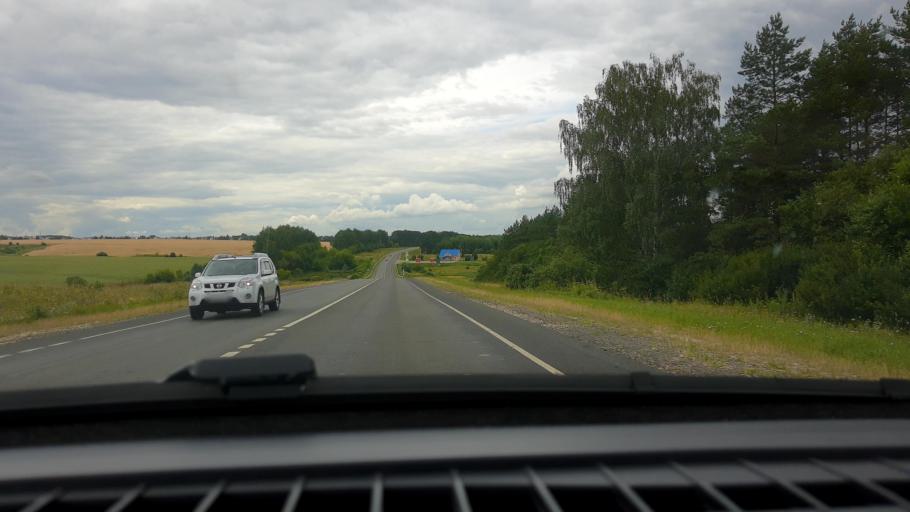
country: RU
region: Nizjnij Novgorod
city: Bol'shoye Murashkino
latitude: 55.7932
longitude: 44.8126
